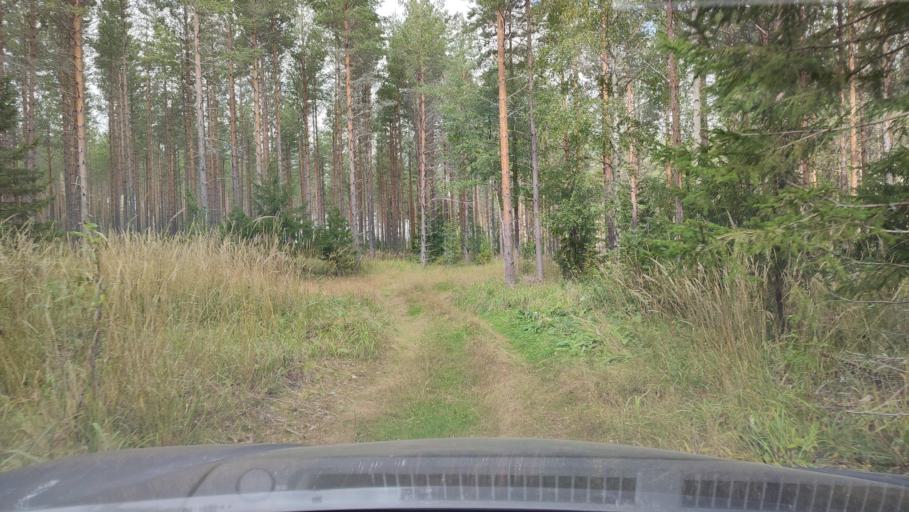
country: FI
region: Southern Ostrobothnia
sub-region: Suupohja
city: Karijoki
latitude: 62.2221
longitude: 21.6182
